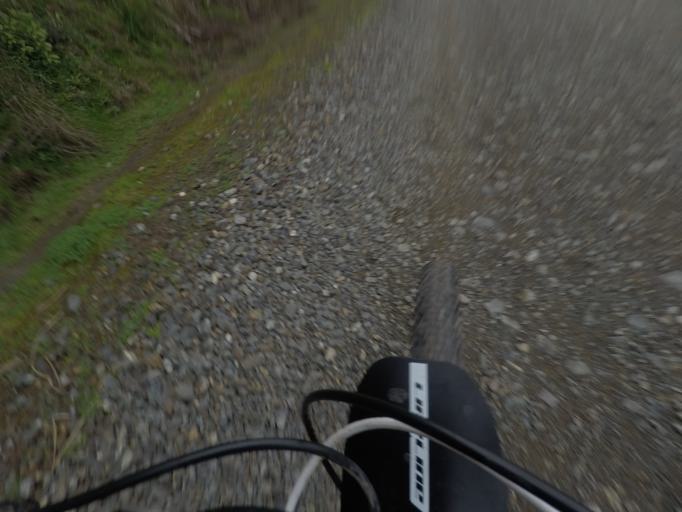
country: NZ
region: Auckland
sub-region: Auckland
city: Muriwai Beach
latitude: -36.7480
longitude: 174.5758
